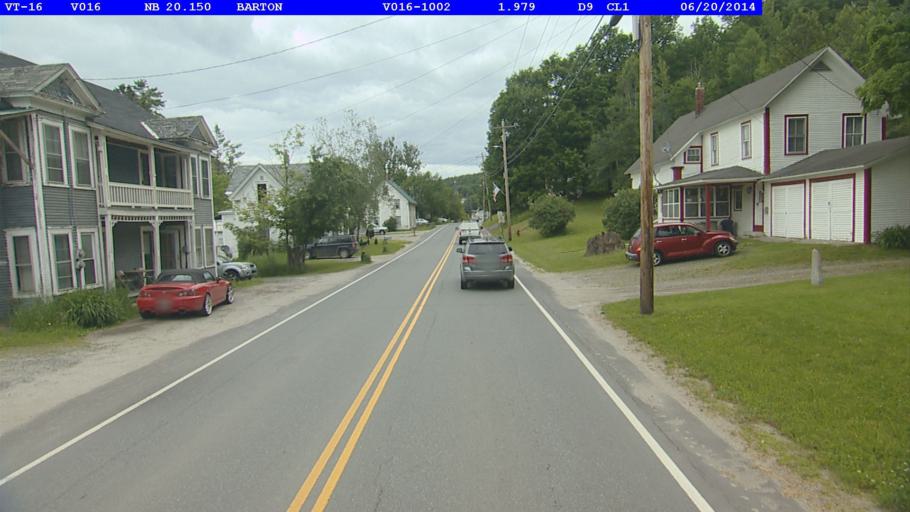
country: US
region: Vermont
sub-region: Orleans County
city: Newport
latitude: 44.7455
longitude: -72.1809
